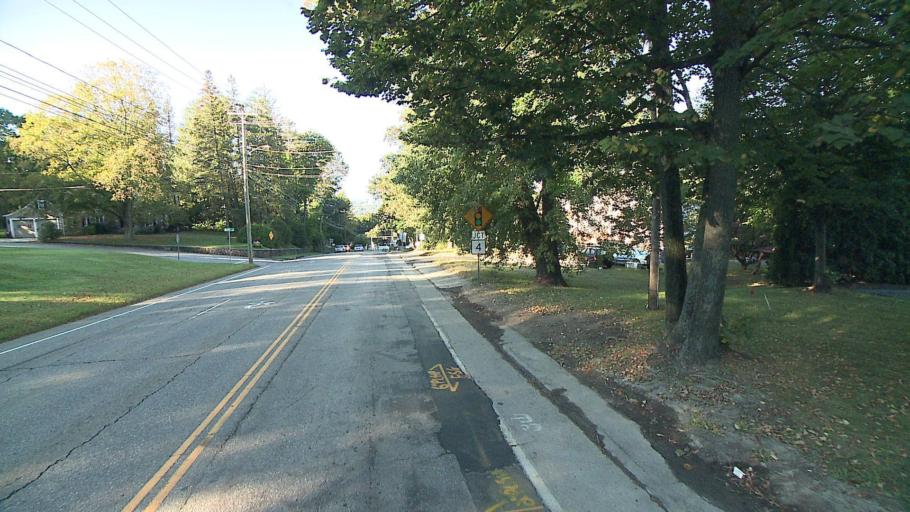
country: US
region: Connecticut
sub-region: Litchfield County
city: Torrington
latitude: 41.8094
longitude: -73.1072
